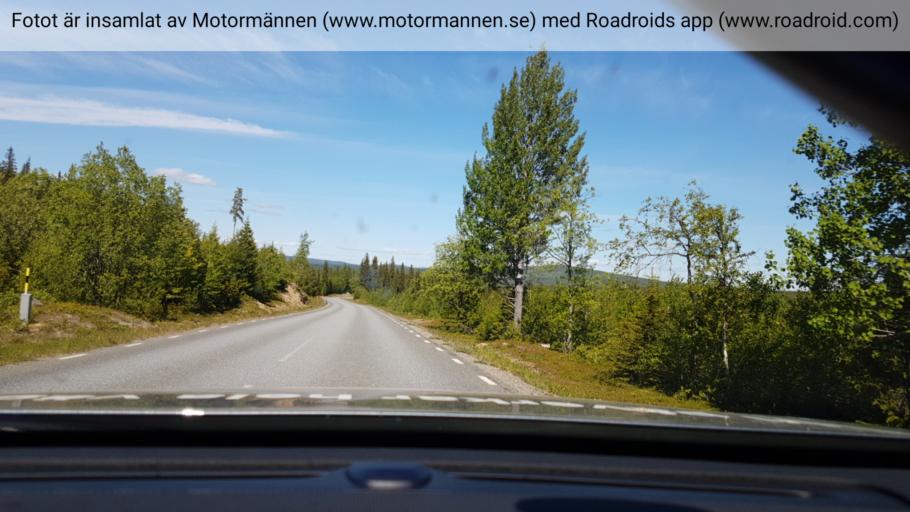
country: SE
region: Vaesterbotten
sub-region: Vilhelmina Kommun
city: Vilhelmina
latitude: 64.6472
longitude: 17.0805
